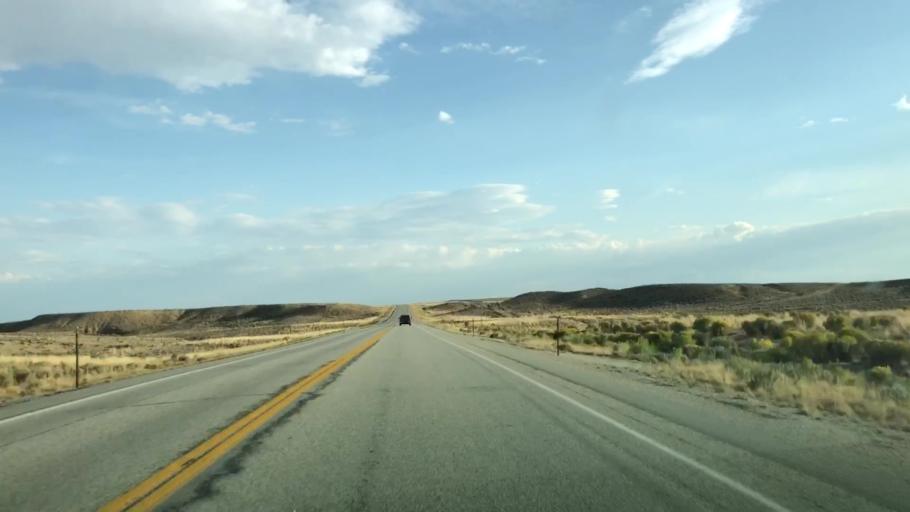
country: US
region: Wyoming
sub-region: Sublette County
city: Pinedale
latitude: 42.3493
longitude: -109.5220
